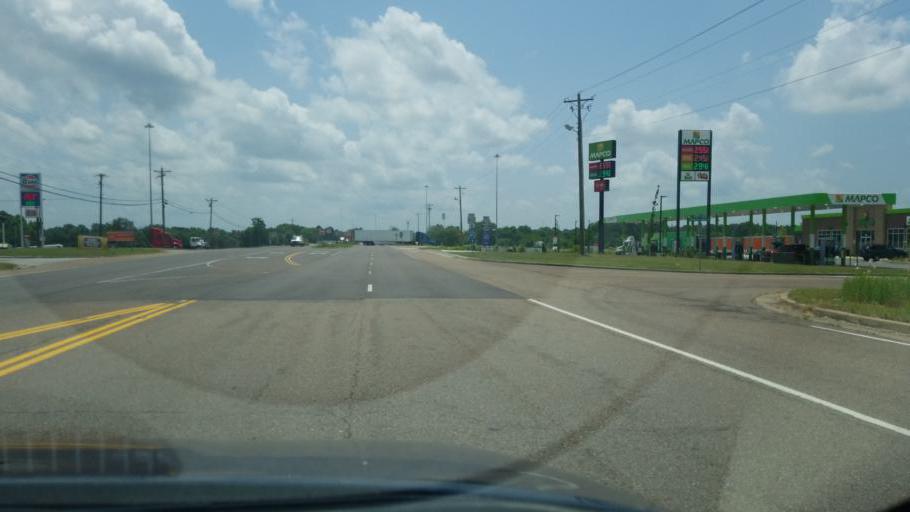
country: US
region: Tennessee
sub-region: Madison County
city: Jackson
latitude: 35.6833
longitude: -88.7407
